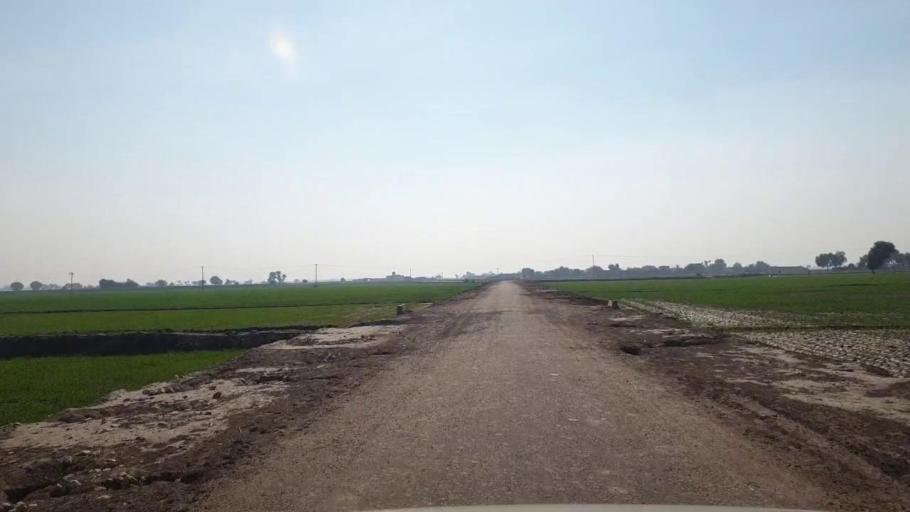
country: PK
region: Sindh
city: Bhan
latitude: 26.6515
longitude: 67.7018
